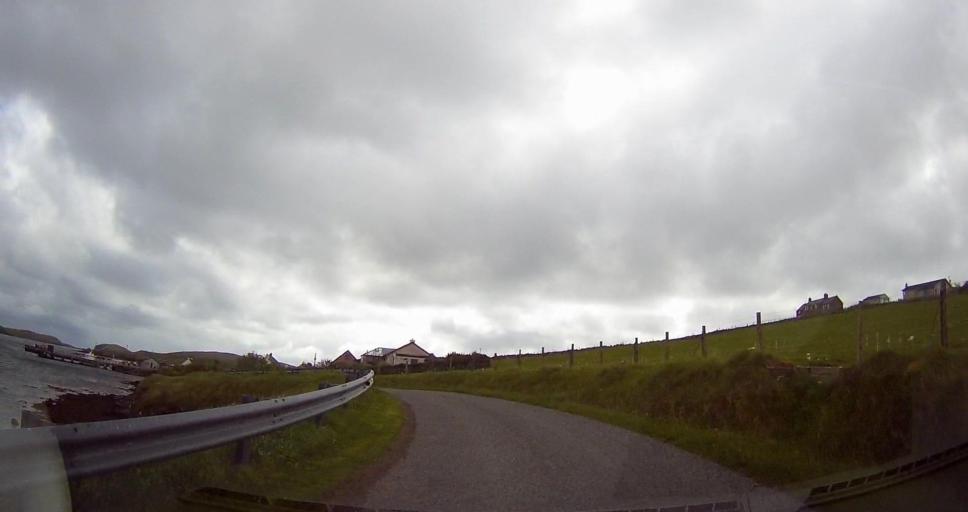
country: GB
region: Scotland
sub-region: Shetland Islands
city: Sandwick
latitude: 60.2264
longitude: -1.5691
